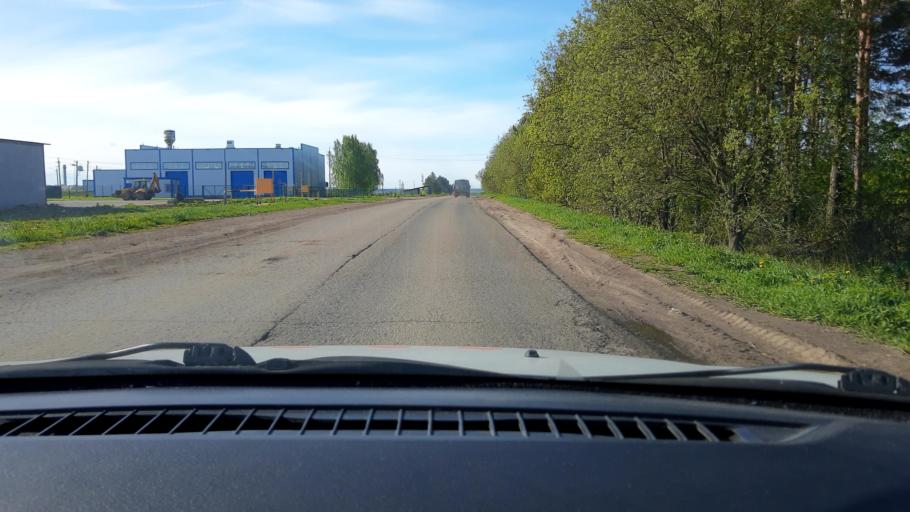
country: RU
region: Nizjnij Novgorod
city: Burevestnik
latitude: 56.1562
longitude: 43.7769
